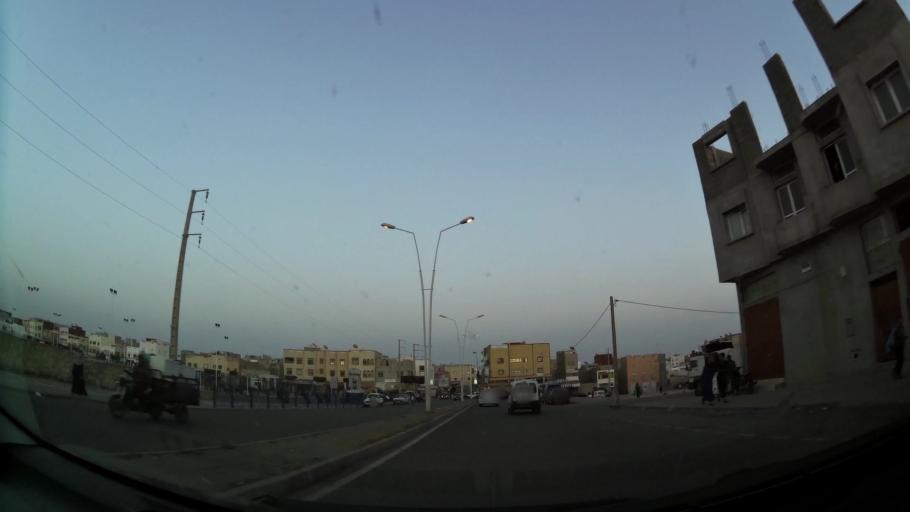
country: MA
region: Souss-Massa-Draa
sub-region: Inezgane-Ait Mellou
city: Inezgane
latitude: 30.3764
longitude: -9.4961
